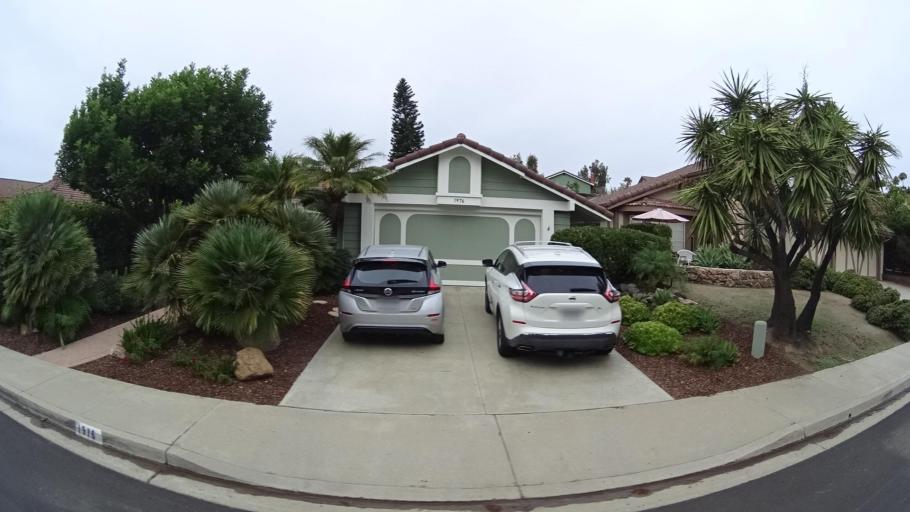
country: US
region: California
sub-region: San Diego County
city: Rancho San Diego
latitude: 32.7576
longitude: -116.9125
